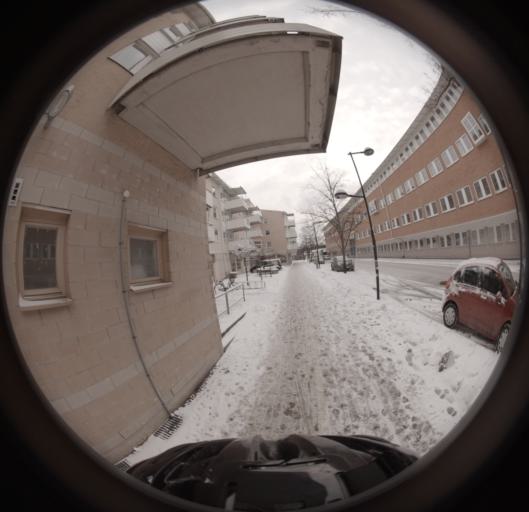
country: SE
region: Stockholm
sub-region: Sollentuna Kommun
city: Sollentuna
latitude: 59.4313
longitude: 17.9466
